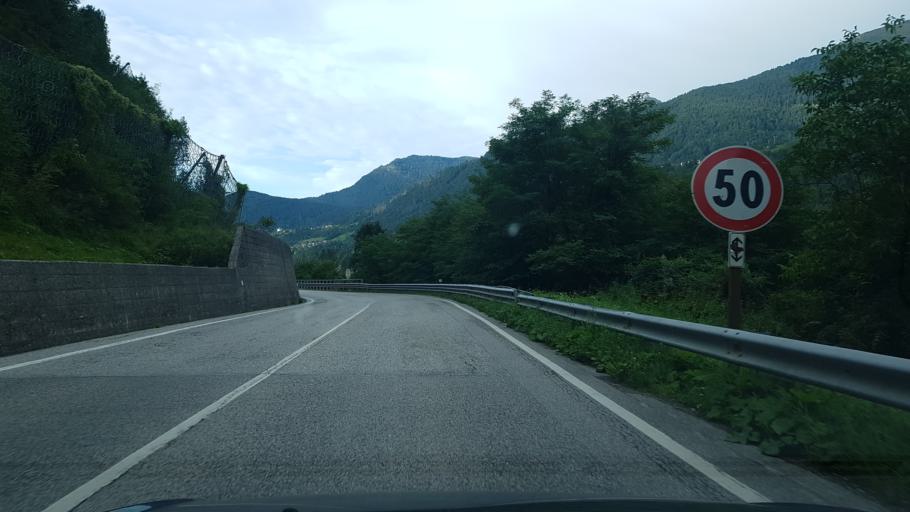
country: IT
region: Friuli Venezia Giulia
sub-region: Provincia di Udine
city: Comeglians
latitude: 46.5096
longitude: 12.8662
